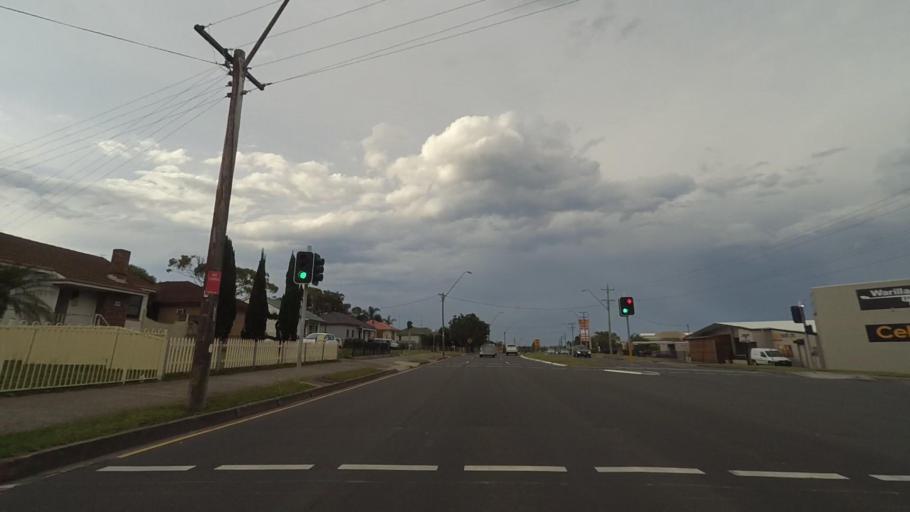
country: AU
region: New South Wales
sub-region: Shellharbour
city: Lake Illawarra
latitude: -34.5484
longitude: 150.8610
